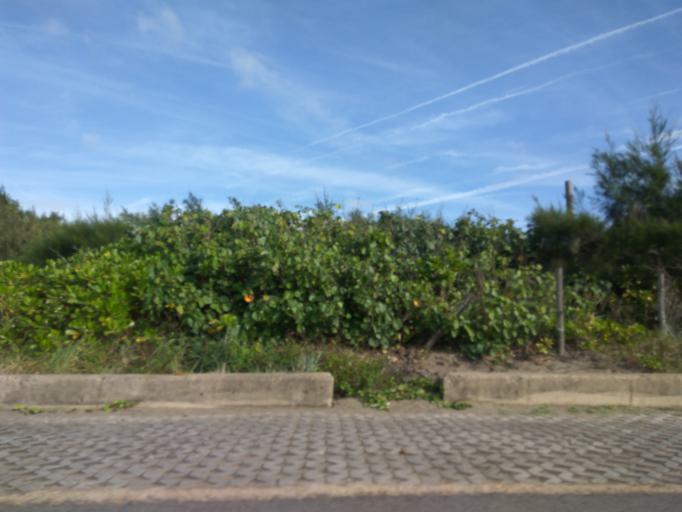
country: TW
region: Taiwan
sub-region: Hsinchu
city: Zhubei
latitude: 24.9855
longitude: 121.0162
